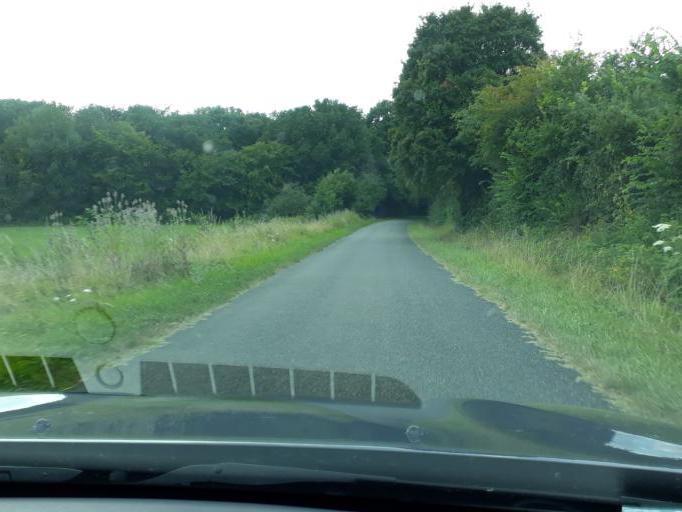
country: FR
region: Centre
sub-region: Departement du Cher
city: Jouet-sur-l'Aubois
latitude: 46.9788
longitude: 2.9365
